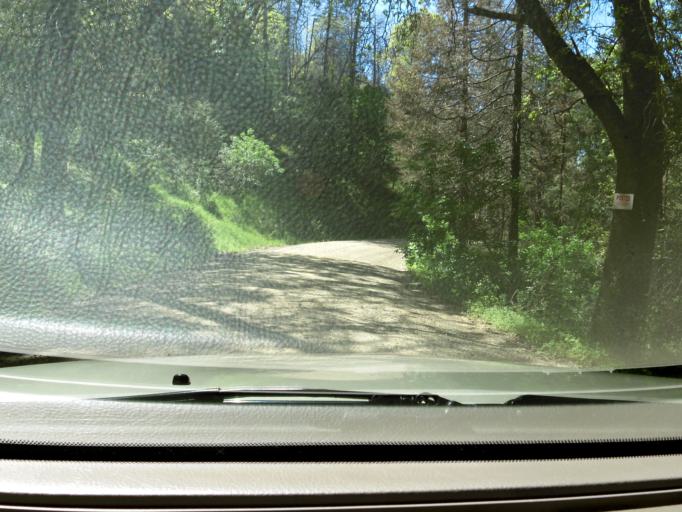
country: US
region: California
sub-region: Madera County
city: Oakhurst
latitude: 37.2839
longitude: -119.6189
